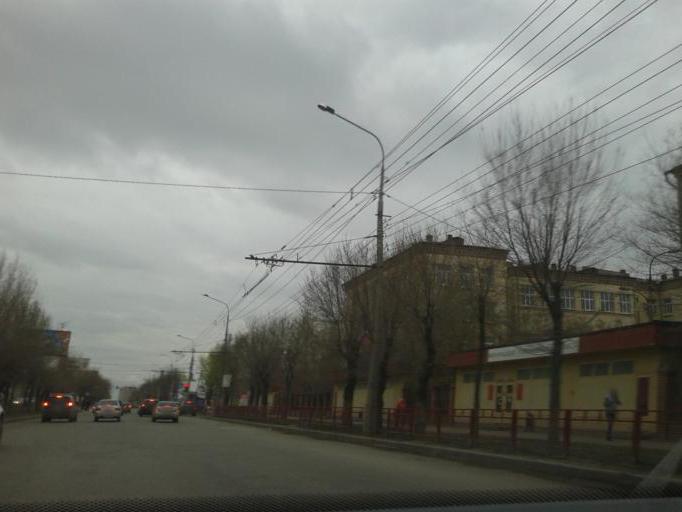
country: RU
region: Volgograd
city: Volgograd
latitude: 48.7368
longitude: 44.4935
